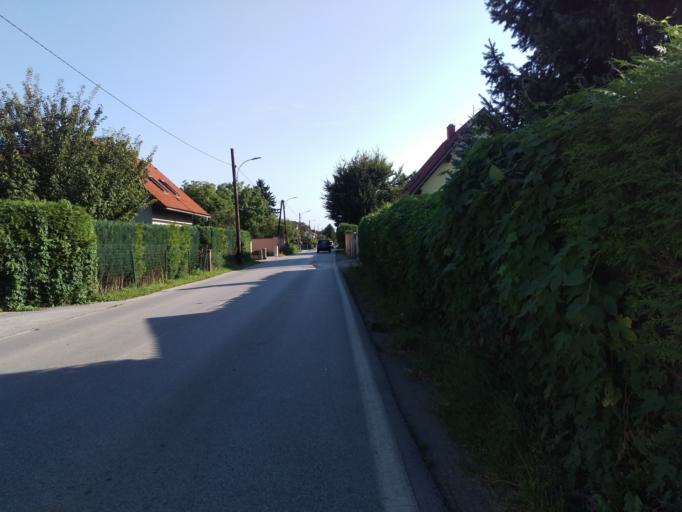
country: AT
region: Styria
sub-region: Politischer Bezirk Graz-Umgebung
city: Feldkirchen bei Graz
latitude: 47.0292
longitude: 15.4416
